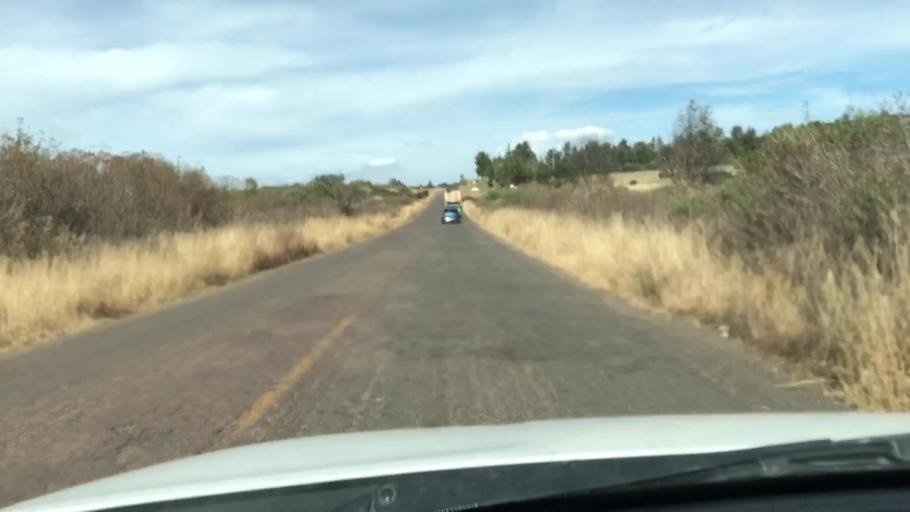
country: MX
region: Jalisco
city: Chiquilistlan
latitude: 20.1662
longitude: -103.7237
